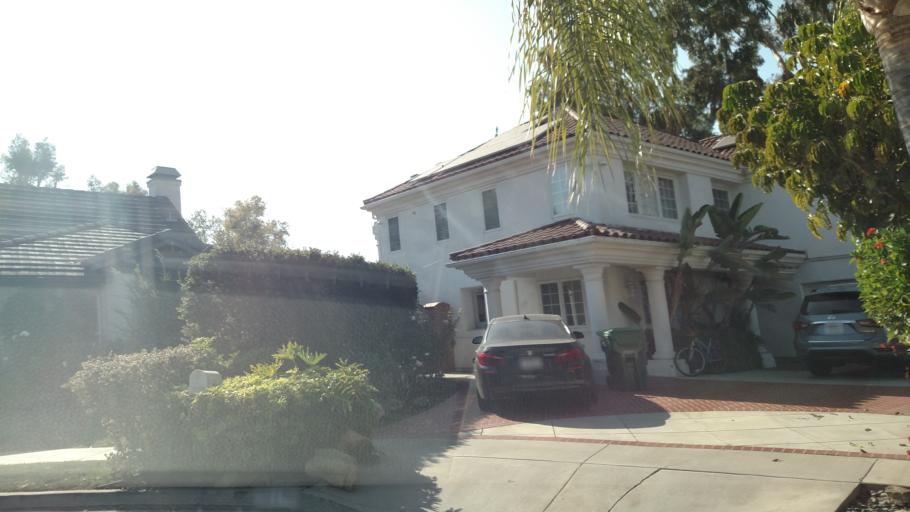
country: US
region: California
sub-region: Orange County
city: Irvine
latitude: 33.6844
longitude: -117.7810
